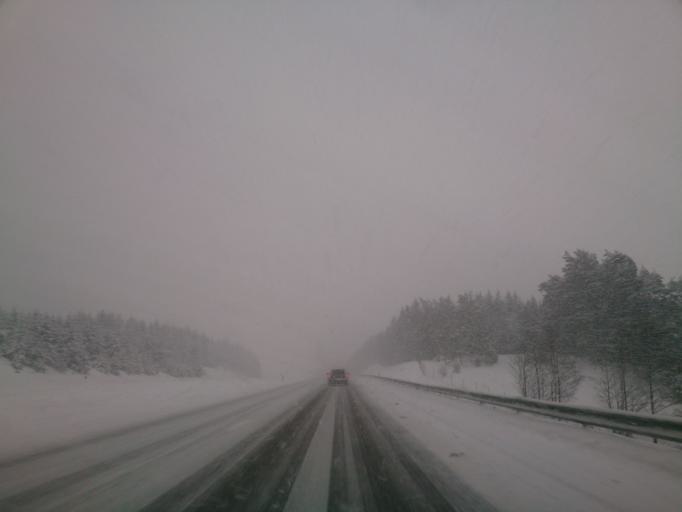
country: SE
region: Soedermanland
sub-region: Nykopings Kommun
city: Stigtomta
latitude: 58.7574
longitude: 16.7163
